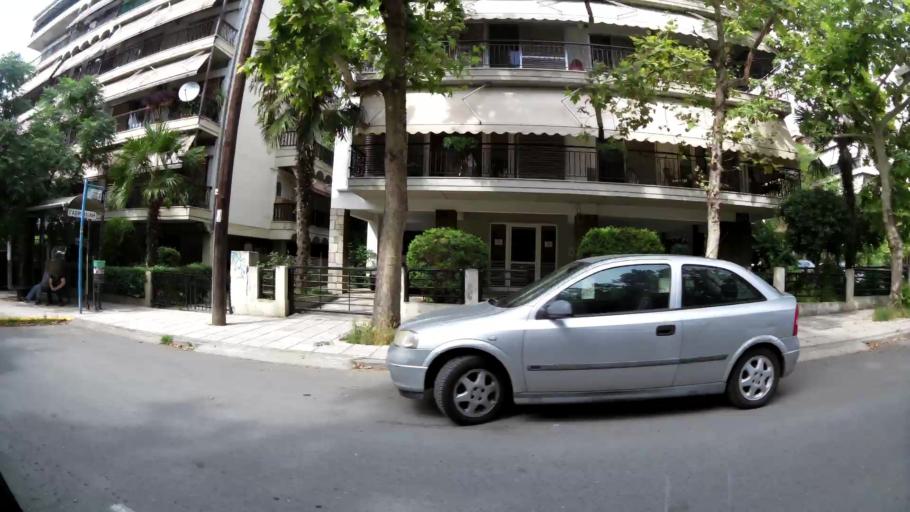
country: GR
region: Central Macedonia
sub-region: Nomos Thessalonikis
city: Kalamaria
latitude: 40.5898
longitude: 22.9515
